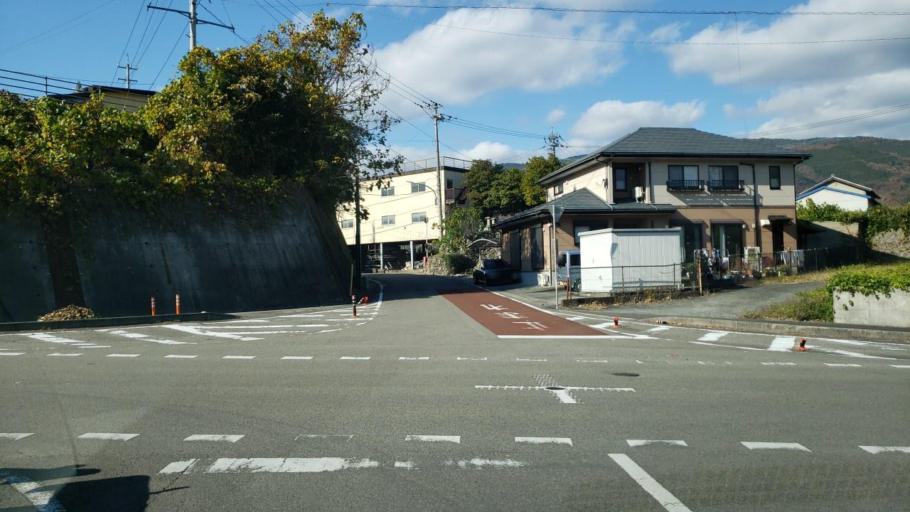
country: JP
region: Tokushima
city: Wakimachi
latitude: 34.0407
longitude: 134.0280
